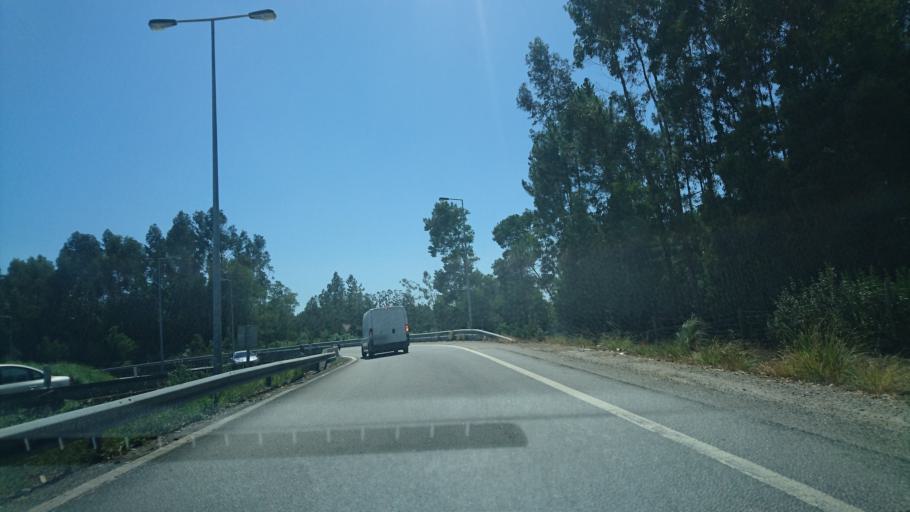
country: PT
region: Aveiro
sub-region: Espinho
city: Souto
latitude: 40.9724
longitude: -8.6113
